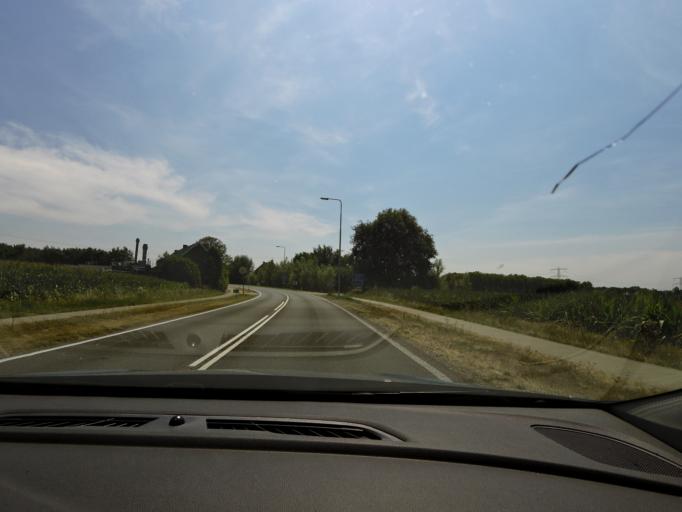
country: NL
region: Limburg
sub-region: Gemeente Leudal
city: Haelen
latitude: 51.2177
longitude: 5.9240
